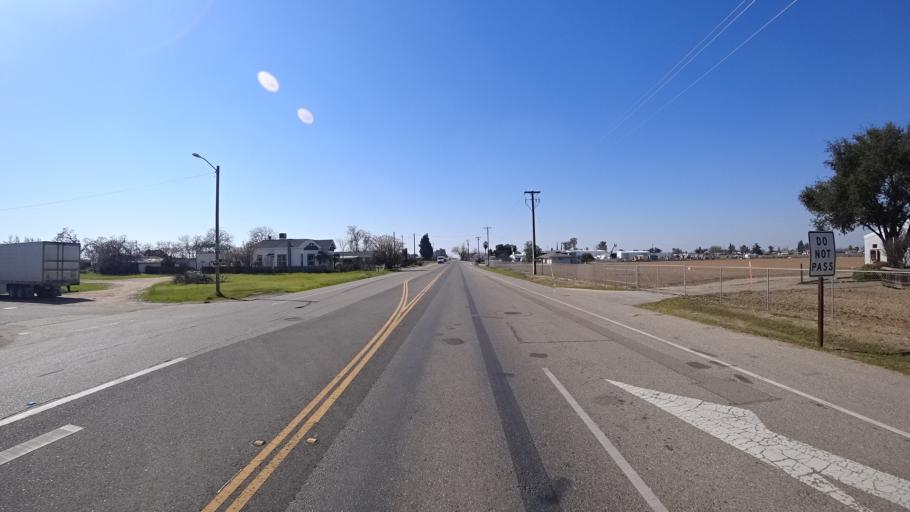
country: US
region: California
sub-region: Fresno County
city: West Park
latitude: 36.7358
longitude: -119.8315
